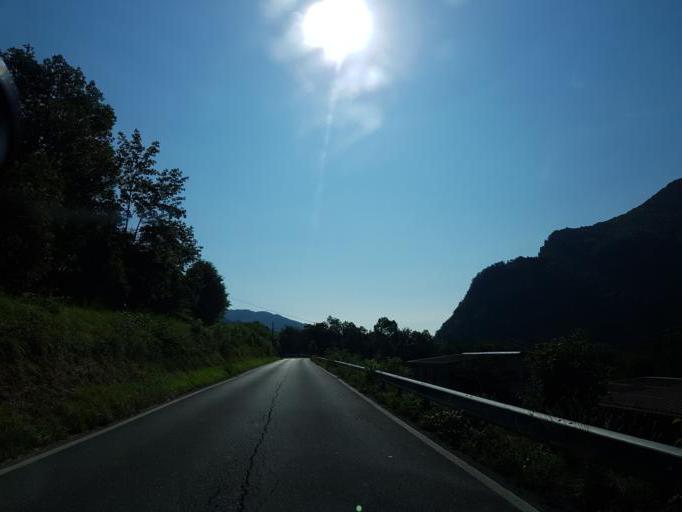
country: IT
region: Piedmont
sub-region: Provincia di Cuneo
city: San Damiano Macra
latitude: 44.4883
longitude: 7.2500
